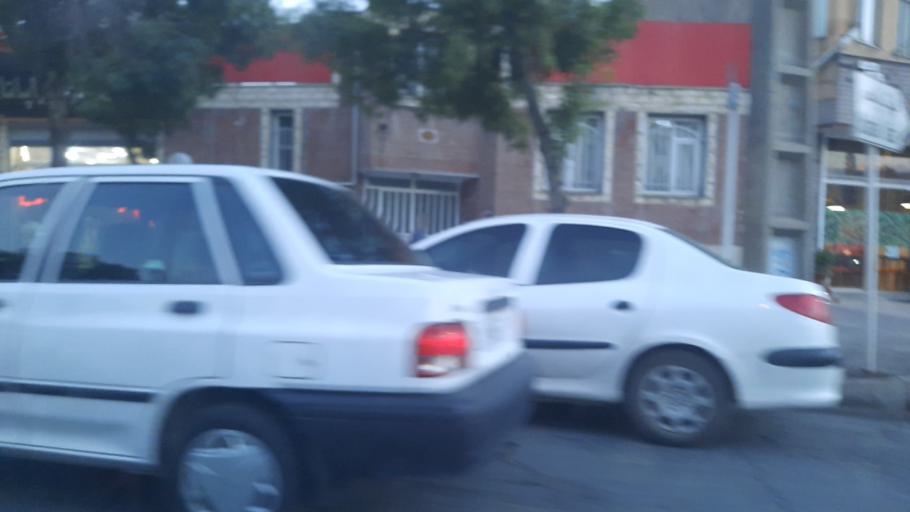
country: IR
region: Markazi
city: Arak
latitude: 34.0764
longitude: 49.6985
